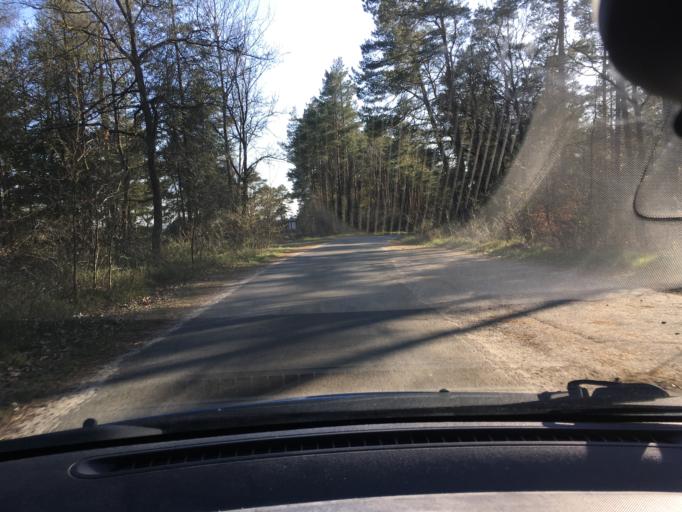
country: DE
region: Lower Saxony
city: Bispingen
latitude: 53.1072
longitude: 10.0100
